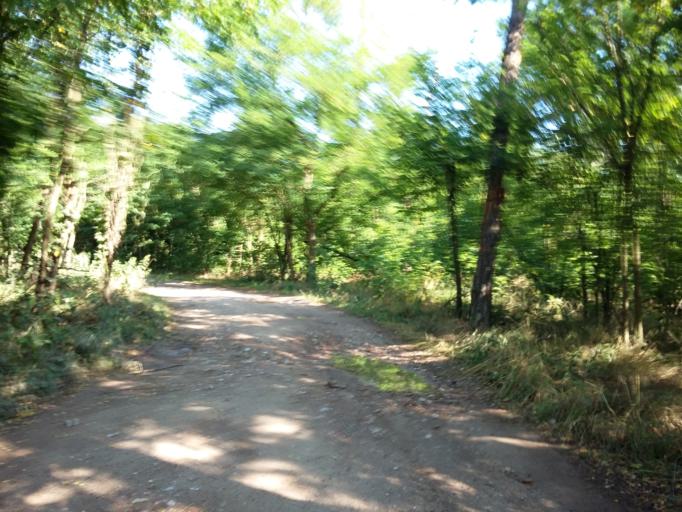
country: AT
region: Lower Austria
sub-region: Politischer Bezirk Ganserndorf
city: Drosing
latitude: 48.4975
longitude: 16.9582
